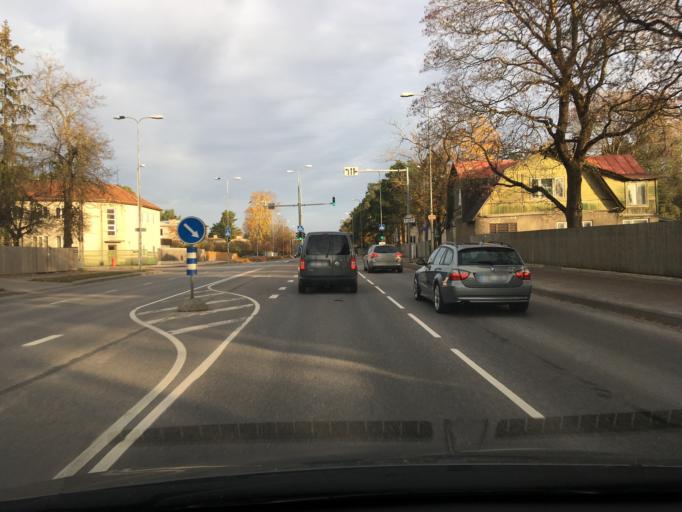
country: EE
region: Harju
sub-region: Tallinna linn
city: Tallinn
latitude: 59.3820
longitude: 24.7176
